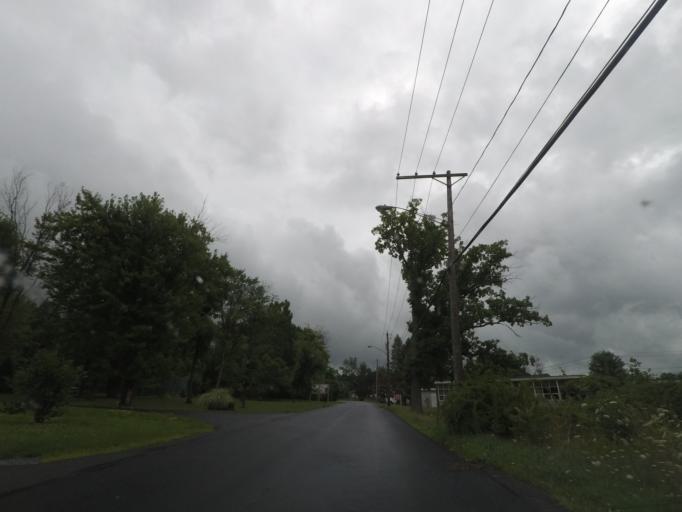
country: US
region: New York
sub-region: Rensselaer County
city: Rensselaer
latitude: 42.6327
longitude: -73.7347
